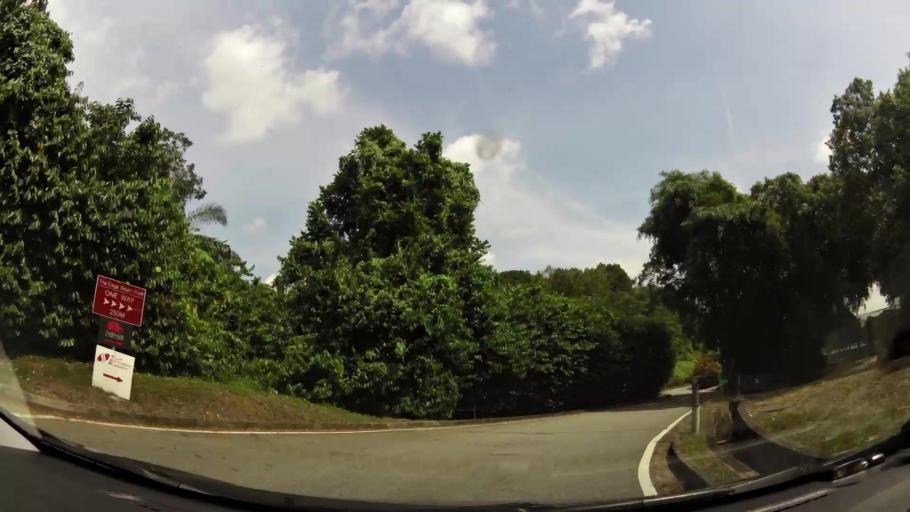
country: SG
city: Singapore
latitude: 1.3425
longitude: 103.7921
